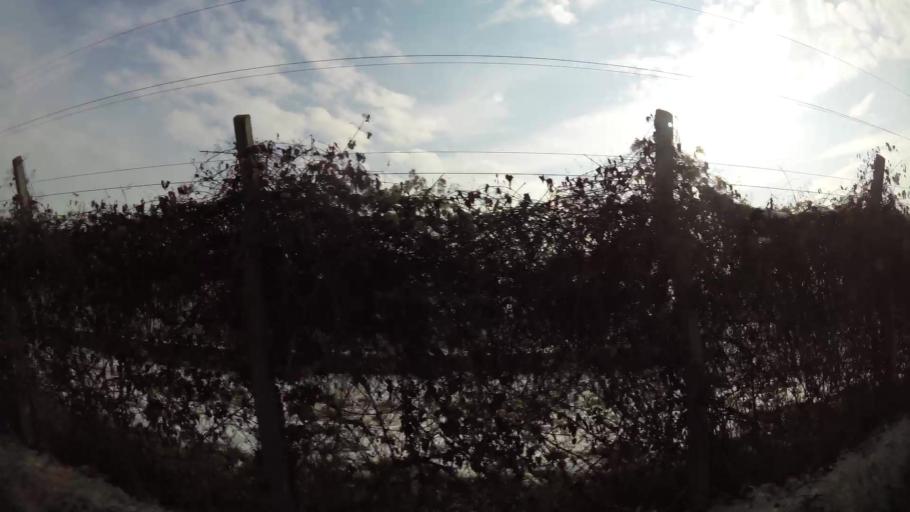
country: MK
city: Krushopek
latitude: 42.0135
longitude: 21.3626
